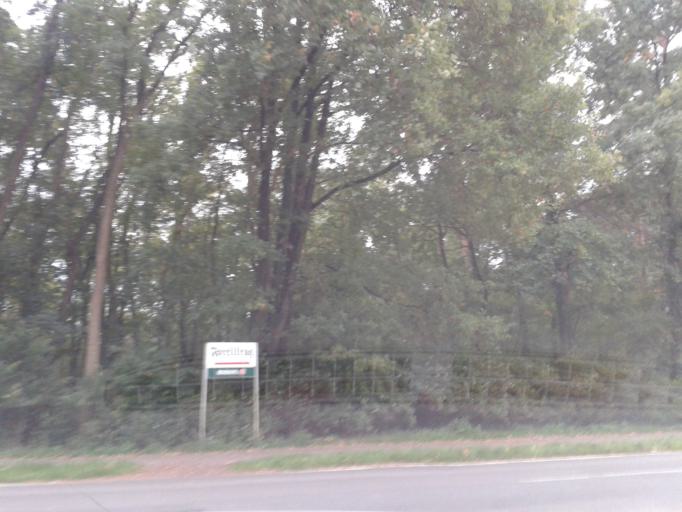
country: DE
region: North Rhine-Westphalia
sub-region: Regierungsbezirk Detmold
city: Augustdorf
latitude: 51.8709
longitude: 8.6920
